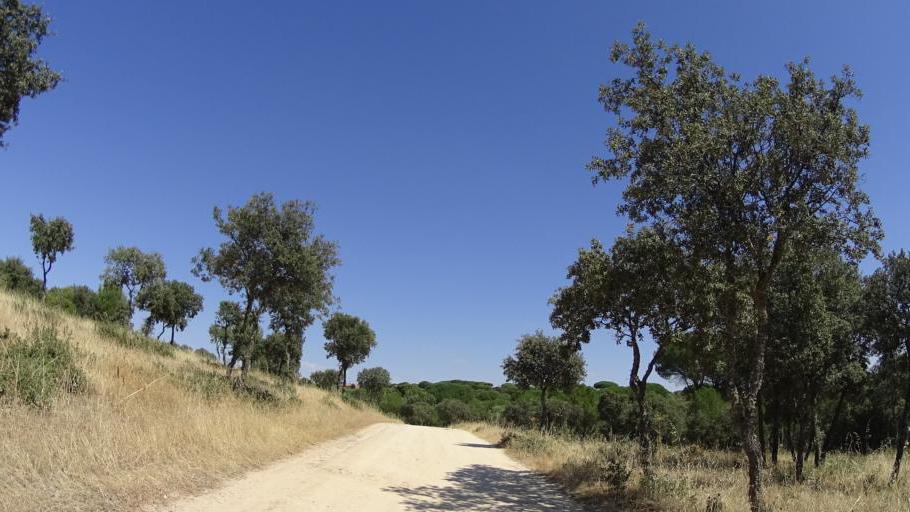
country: ES
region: Madrid
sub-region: Provincia de Madrid
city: Boadilla del Monte
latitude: 40.4317
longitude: -3.8551
